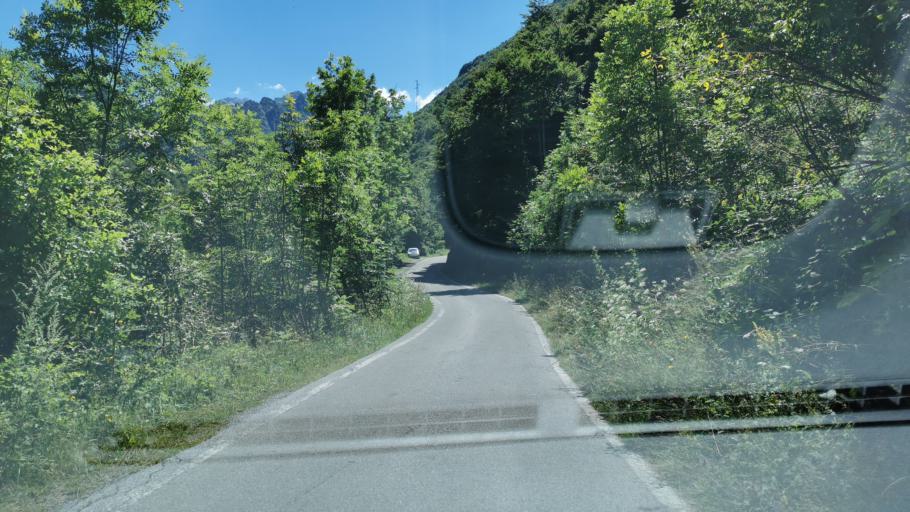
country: IT
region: Piedmont
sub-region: Provincia di Cuneo
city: Entracque
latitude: 44.1865
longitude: 7.3837
